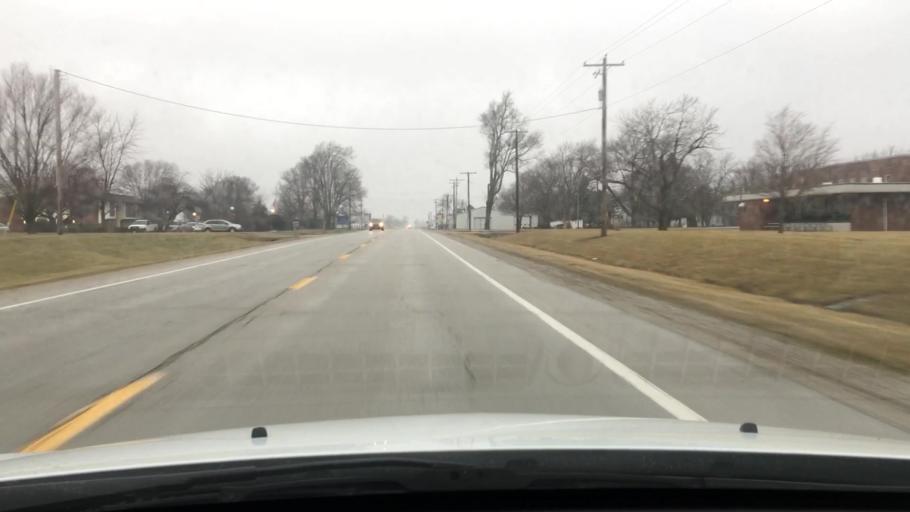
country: US
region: Illinois
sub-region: Livingston County
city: Flanagan
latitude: 40.8711
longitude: -88.8570
